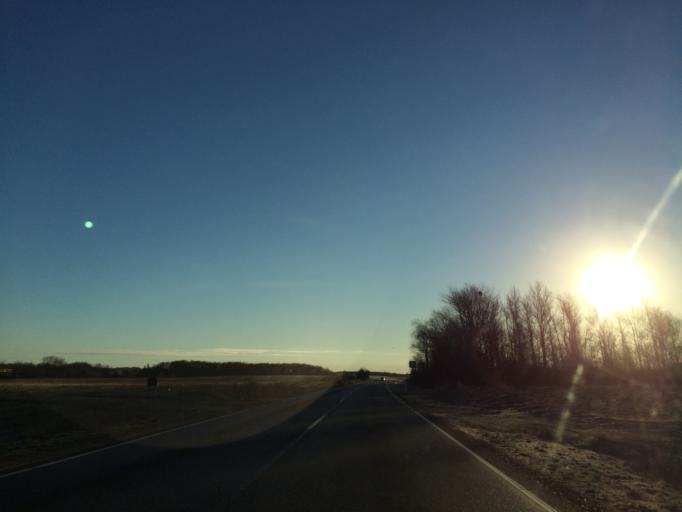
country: DK
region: Central Jutland
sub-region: Lemvig Kommune
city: Lemvig
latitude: 56.5287
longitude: 8.3778
